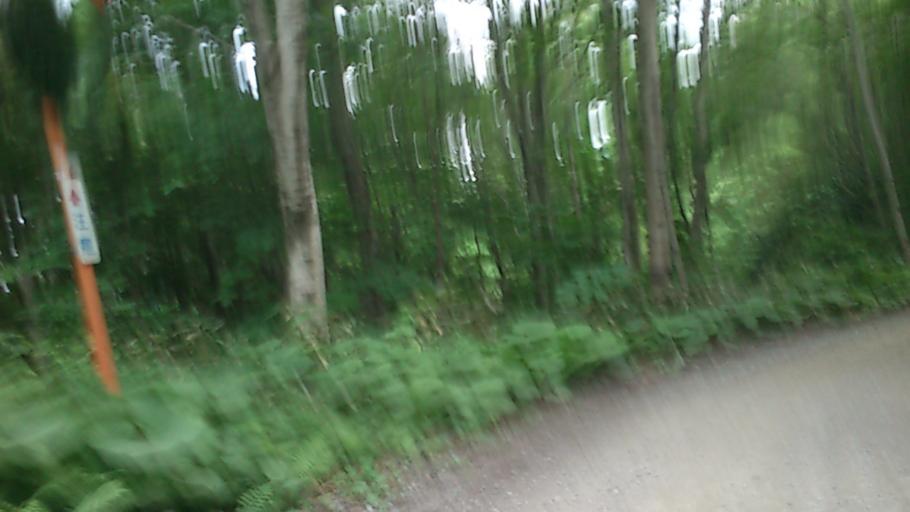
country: JP
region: Aomori
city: Hirosaki
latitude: 40.5542
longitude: 140.1804
